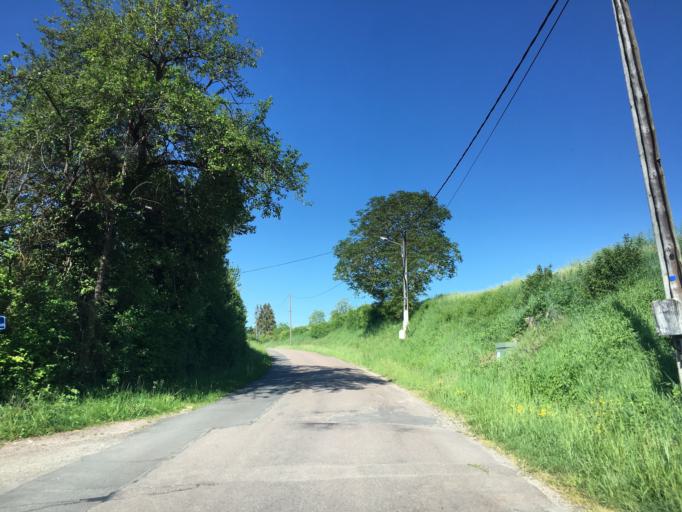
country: FR
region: Bourgogne
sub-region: Departement de l'Yonne
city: Aillant-sur-Tholon
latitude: 47.8279
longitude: 3.3397
